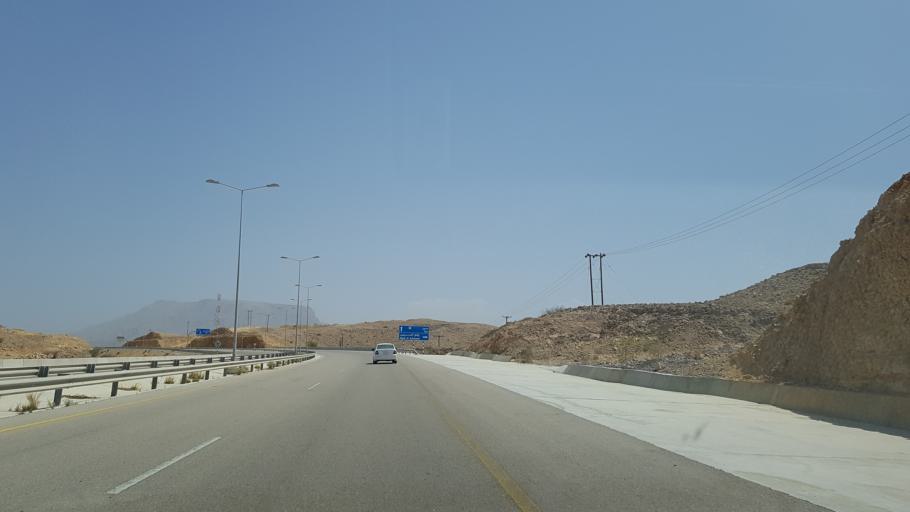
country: OM
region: Ash Sharqiyah
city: Al Qabil
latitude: 23.1143
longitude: 58.9782
